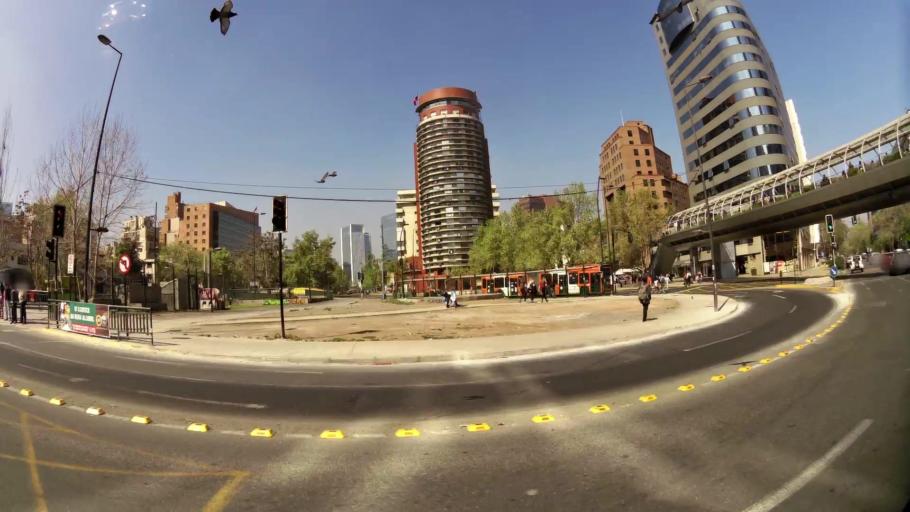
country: CL
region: Santiago Metropolitan
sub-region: Provincia de Santiago
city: Villa Presidente Frei, Nunoa, Santiago, Chile
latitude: -33.4174
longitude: -70.6051
